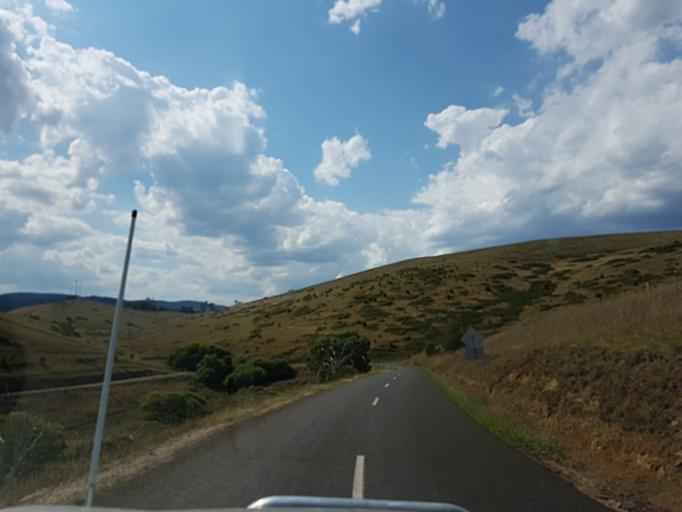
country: AU
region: Victoria
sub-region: East Gippsland
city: Lakes Entrance
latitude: -37.5005
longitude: 148.1893
